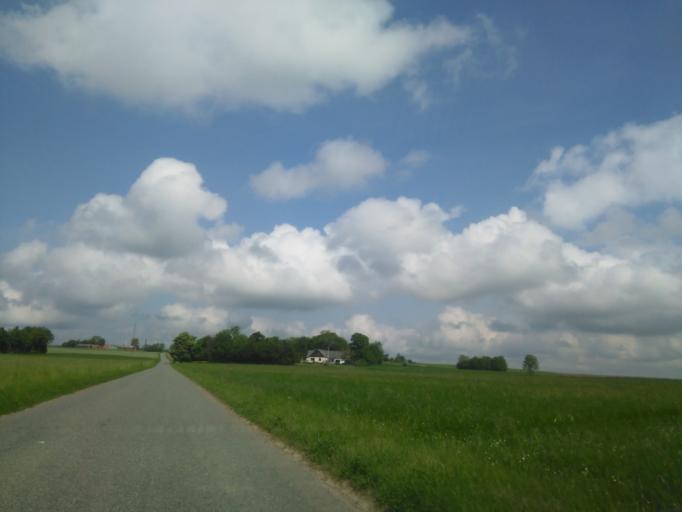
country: DK
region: Central Jutland
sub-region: Arhus Kommune
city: Sabro
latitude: 56.1949
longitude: 10.0032
